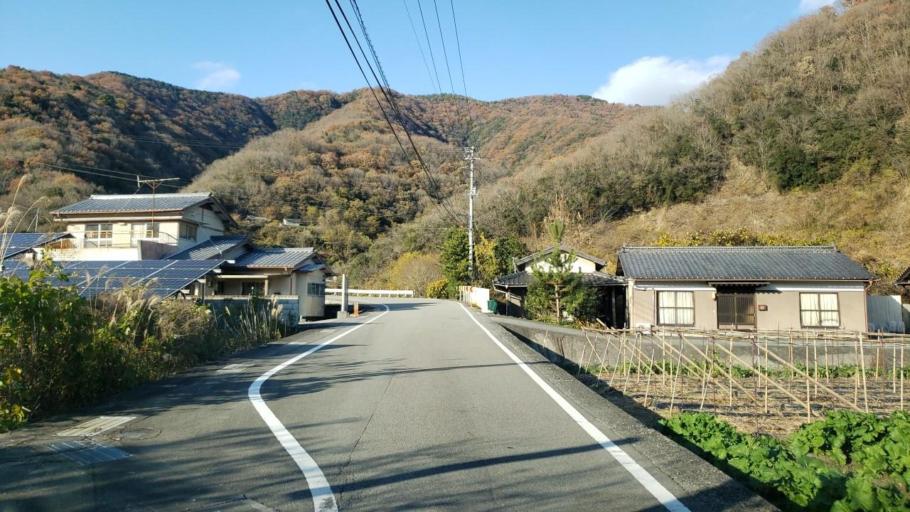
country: JP
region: Tokushima
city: Wakimachi
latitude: 34.0743
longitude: 134.0836
